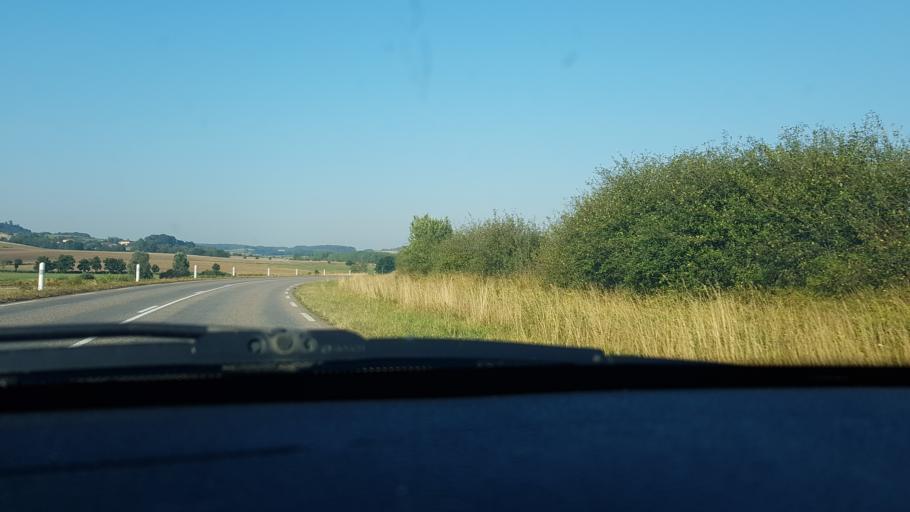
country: FR
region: Lorraine
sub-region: Departement des Vosges
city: Charmes
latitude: 48.3637
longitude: 6.2659
